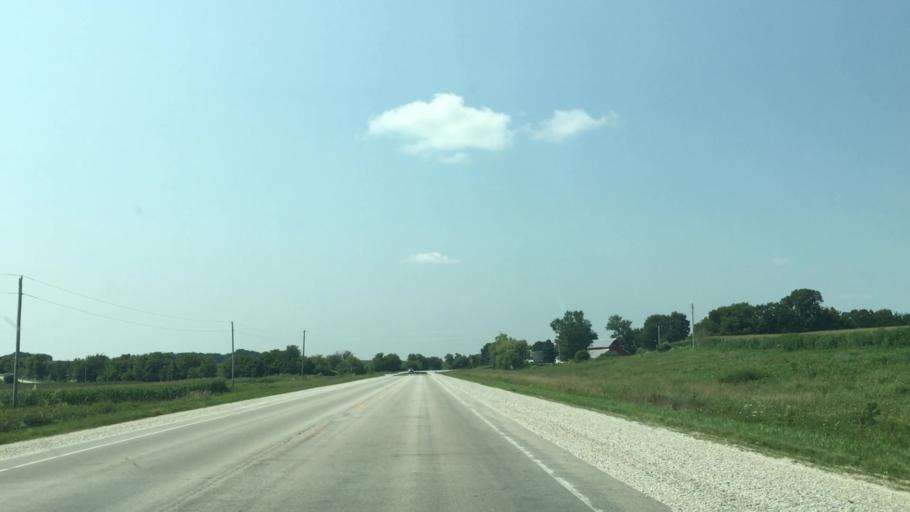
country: US
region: Iowa
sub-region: Winneshiek County
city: Decorah
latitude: 43.4024
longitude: -91.8480
